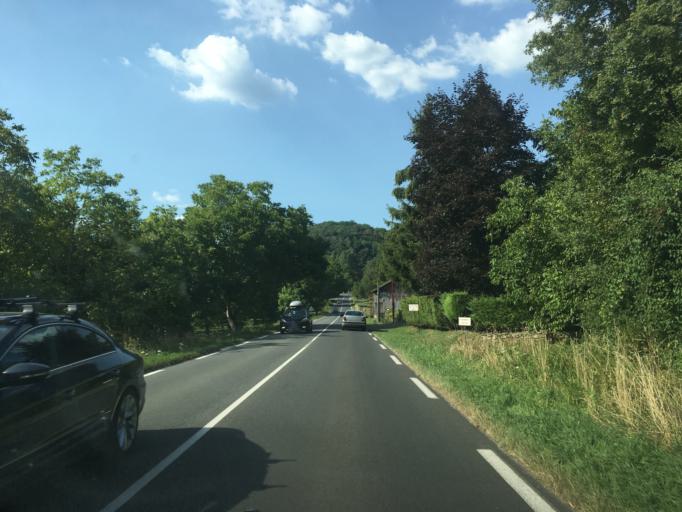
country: FR
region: Aquitaine
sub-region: Departement de la Dordogne
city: Cenac-et-Saint-Julien
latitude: 44.8415
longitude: 1.1710
